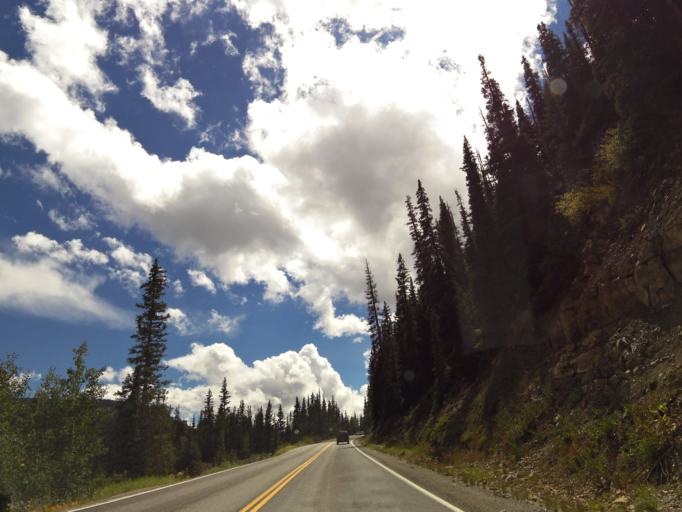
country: US
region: Colorado
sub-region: San Juan County
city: Silverton
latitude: 37.7783
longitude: -107.6713
